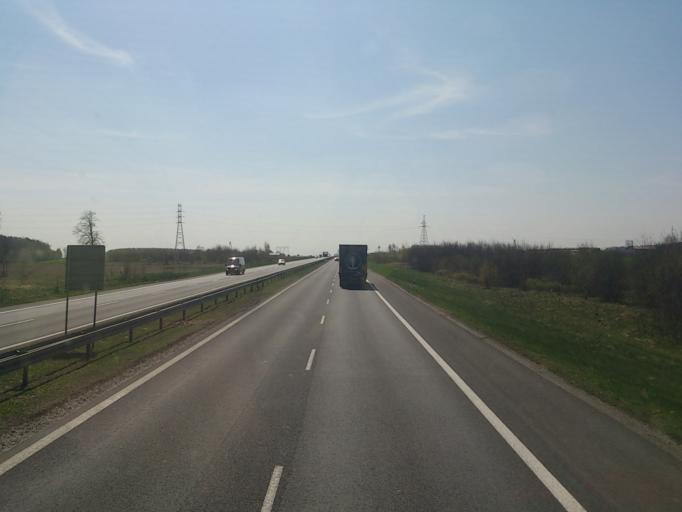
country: PL
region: Lodz Voivodeship
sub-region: Piotrkow Trybunalski
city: Piotrkow Trybunalski
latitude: 51.3993
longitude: 19.6313
